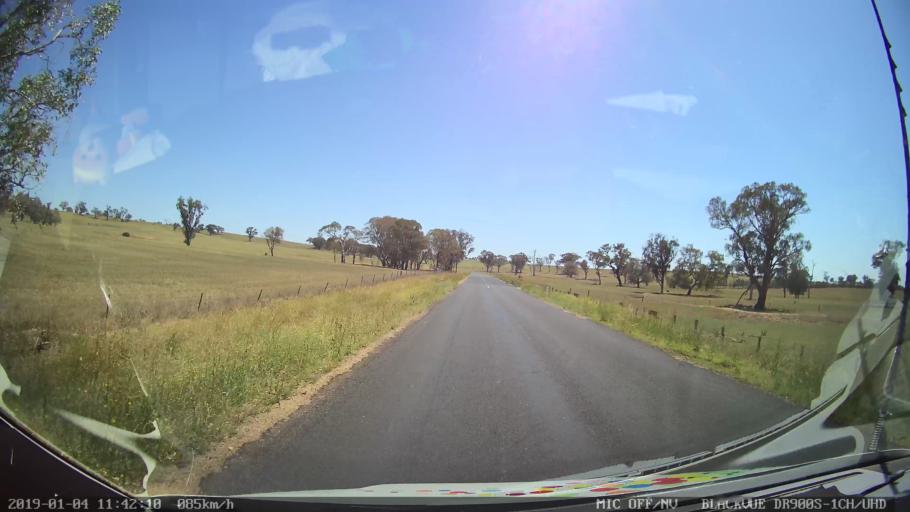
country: AU
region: New South Wales
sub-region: Cabonne
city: Molong
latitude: -32.9849
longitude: 148.7866
